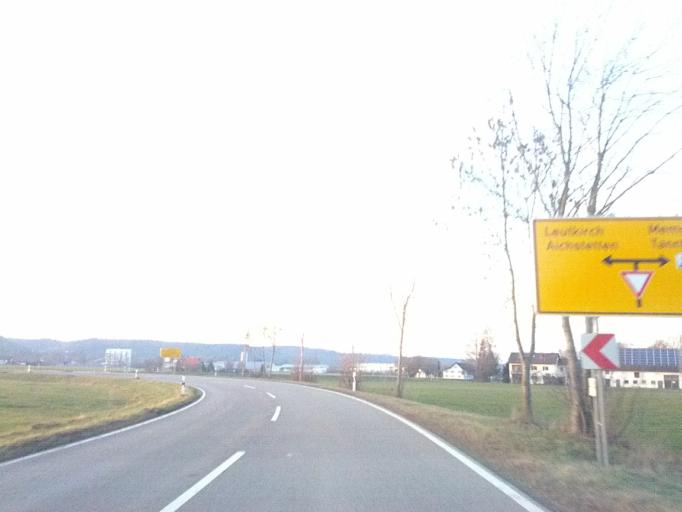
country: DE
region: Baden-Wuerttemberg
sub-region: Tuebingen Region
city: Aitrach
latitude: 47.9245
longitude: 10.1020
